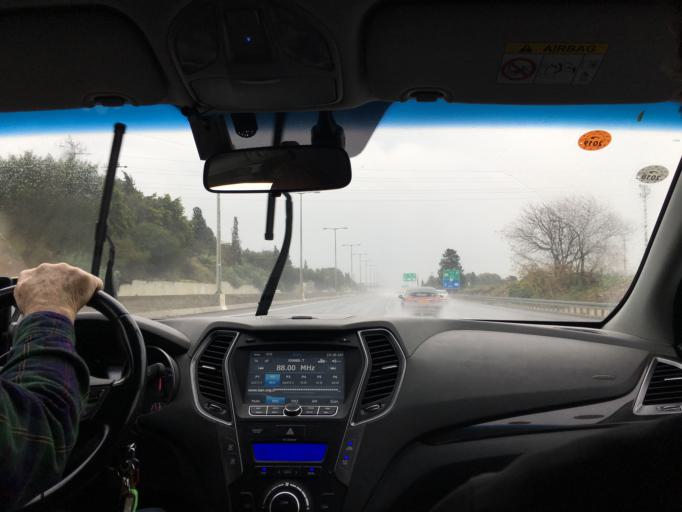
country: IL
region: Tel Aviv
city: Ramat HaSharon
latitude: 32.1303
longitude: 34.8417
